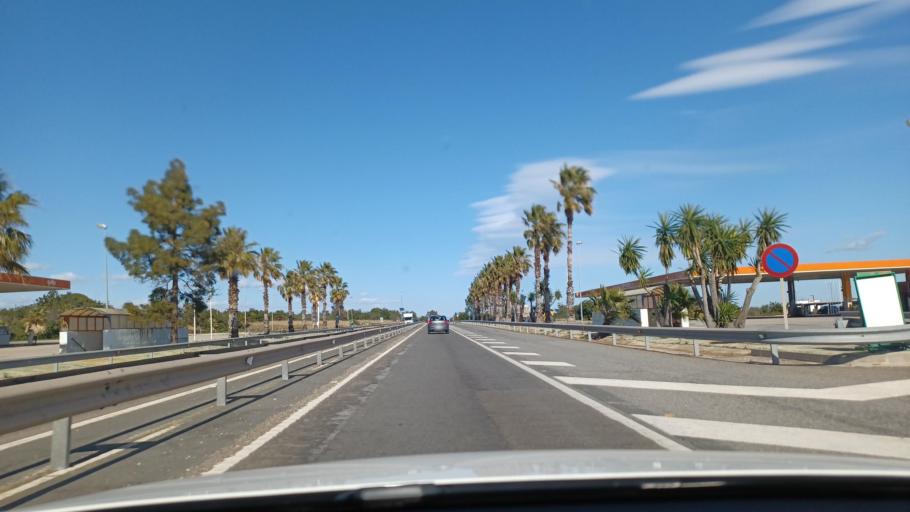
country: ES
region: Catalonia
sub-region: Provincia de Tarragona
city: Sant Carles de la Rapita
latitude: 40.6251
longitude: 0.5782
